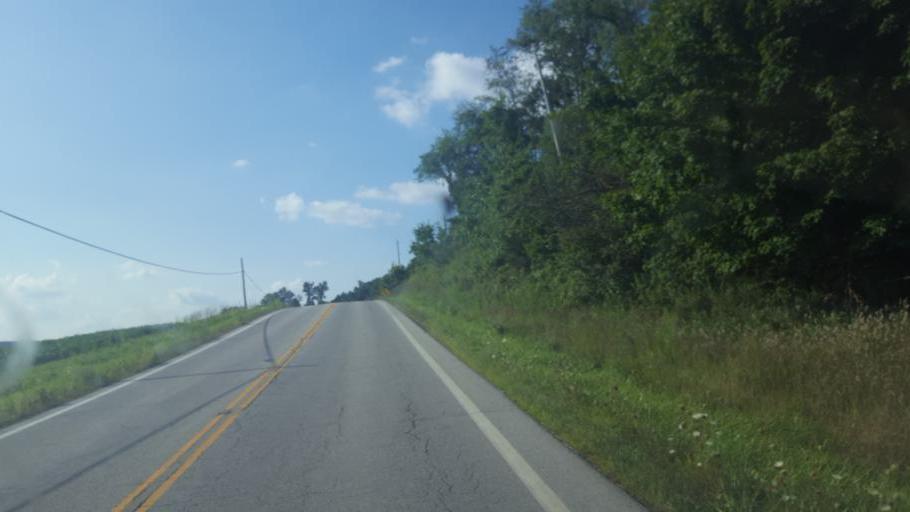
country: US
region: Ohio
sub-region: Sandusky County
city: Bellville
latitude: 40.5804
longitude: -82.4114
